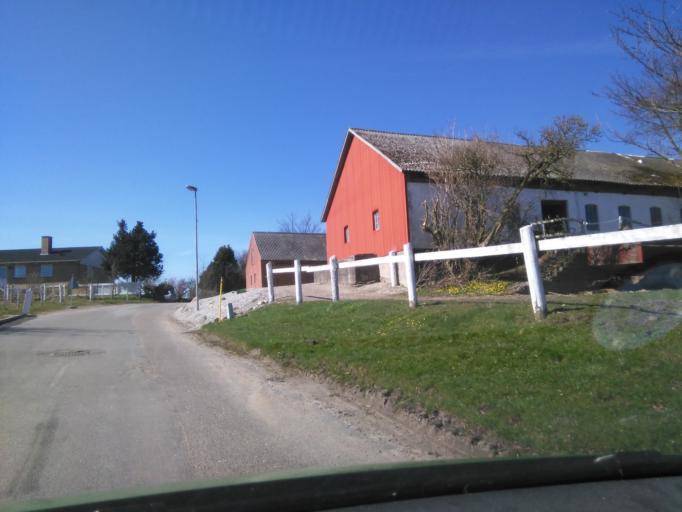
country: DK
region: Central Jutland
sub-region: Arhus Kommune
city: Lystrup
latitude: 56.2421
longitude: 10.1962
